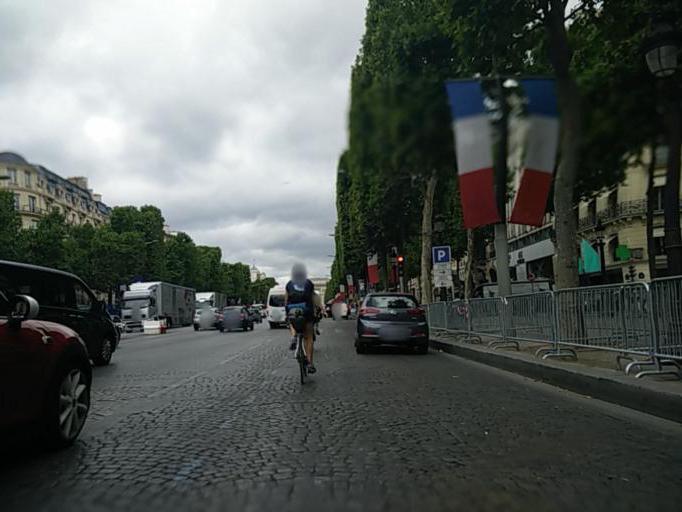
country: FR
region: Ile-de-France
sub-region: Departement des Hauts-de-Seine
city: Levallois-Perret
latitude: 48.8704
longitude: 2.3061
